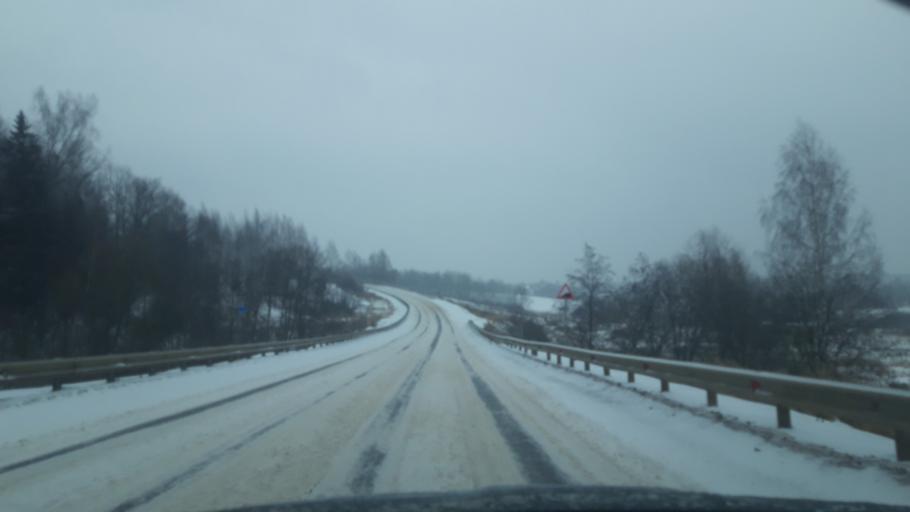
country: RU
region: Moskovskaya
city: Avtopoligon
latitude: 56.2698
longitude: 37.3550
